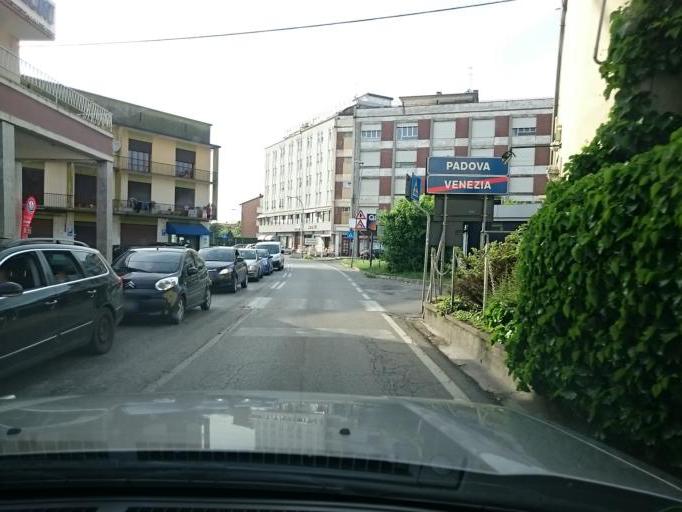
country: IT
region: Veneto
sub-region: Provincia di Padova
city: Oltre Brenta
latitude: 45.4105
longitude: 12.0041
